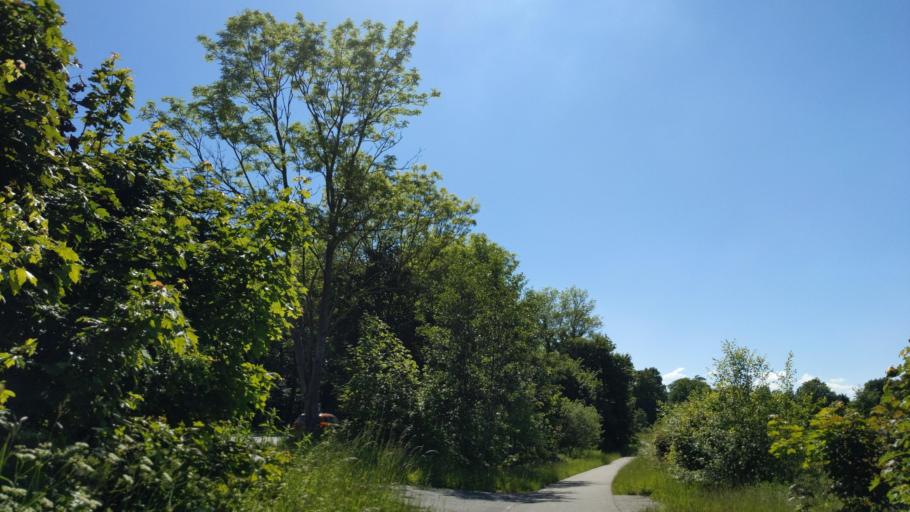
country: DE
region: Schleswig-Holstein
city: Eutin
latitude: 54.1341
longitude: 10.6323
